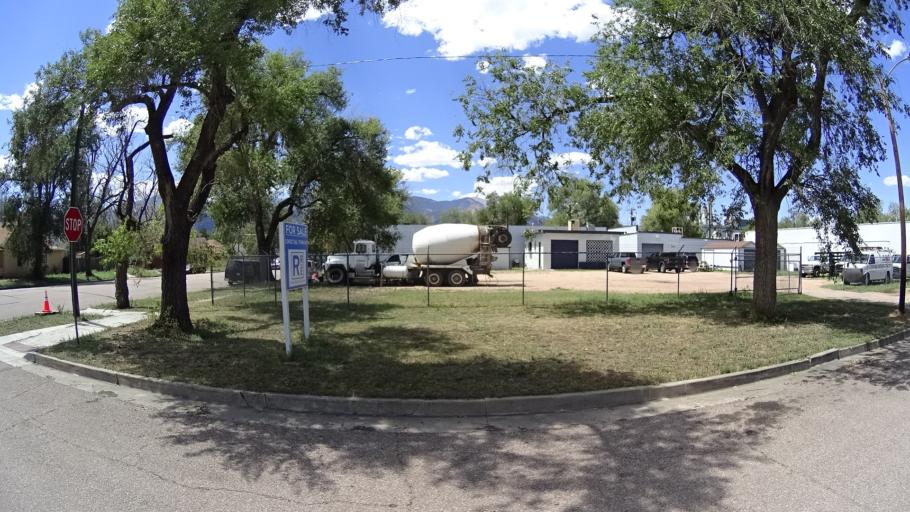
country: US
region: Colorado
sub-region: El Paso County
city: Colorado Springs
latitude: 38.8221
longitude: -104.8278
